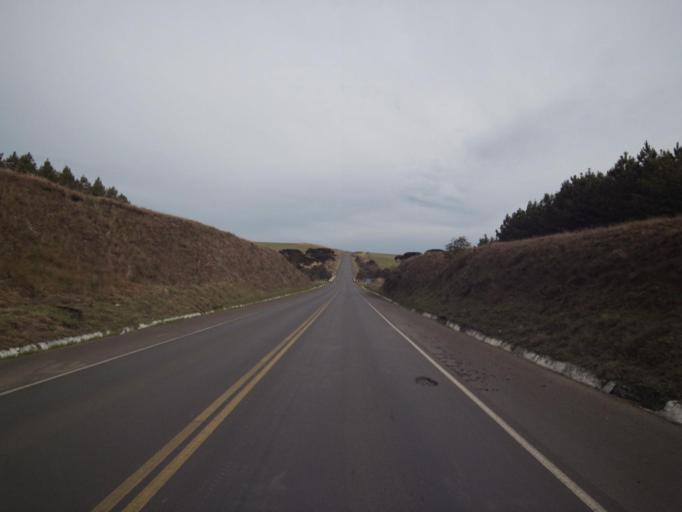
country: BR
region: Parana
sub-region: Palmas
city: Palmas
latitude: -26.7580
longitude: -51.6656
